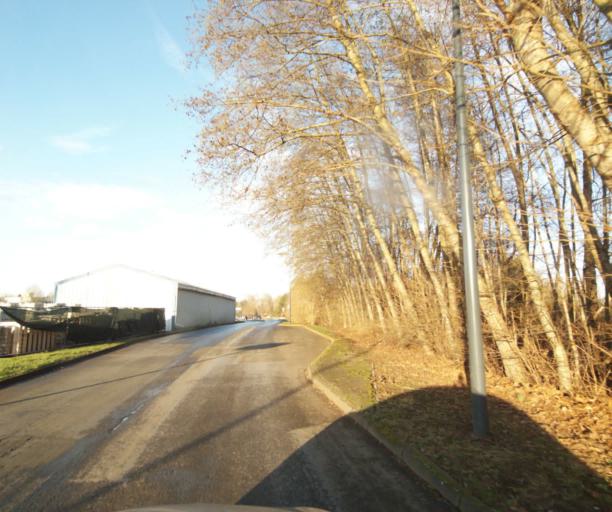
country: FR
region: Nord-Pas-de-Calais
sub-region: Departement du Nord
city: Famars
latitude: 50.3243
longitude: 3.5166
